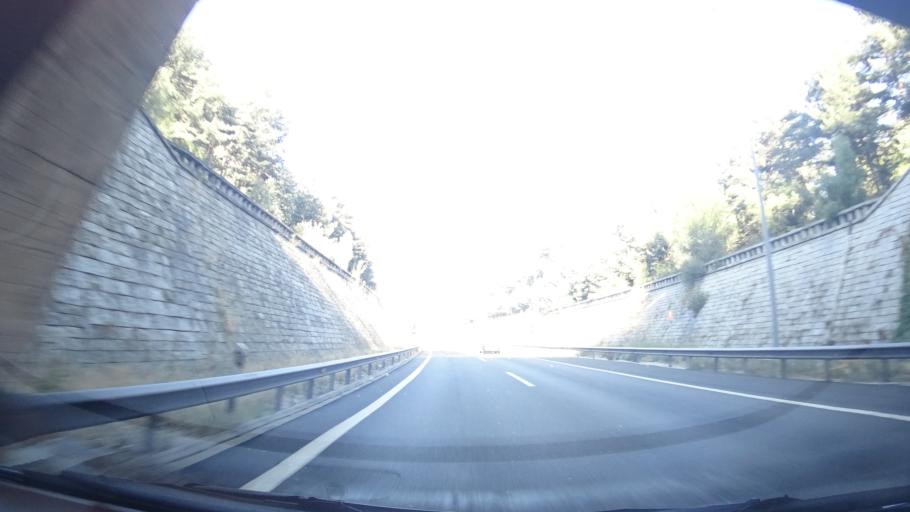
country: ES
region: Madrid
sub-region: Provincia de Madrid
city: Guadarrama
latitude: 40.7168
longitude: -4.1609
